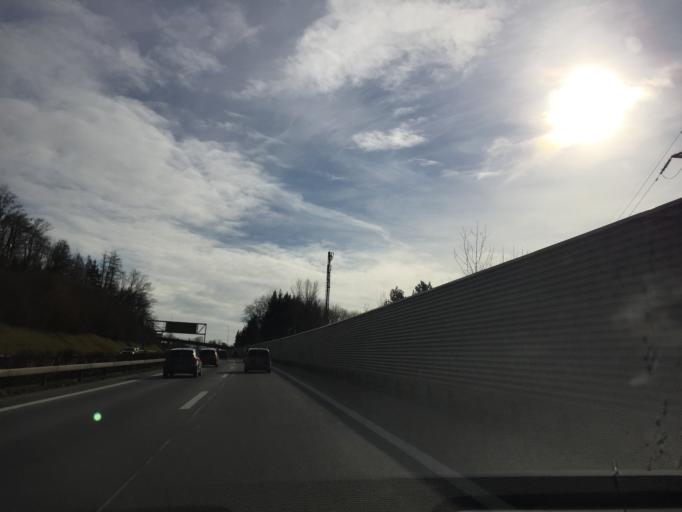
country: CH
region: Zurich
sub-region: Bezirk Horgen
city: Adliswil / Tal
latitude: 47.3190
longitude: 8.5350
